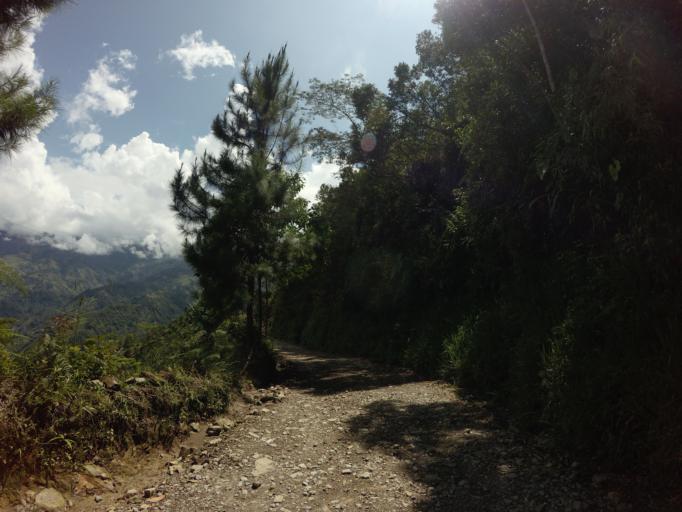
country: CO
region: Caldas
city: Pensilvania
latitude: 5.4897
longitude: -75.1791
